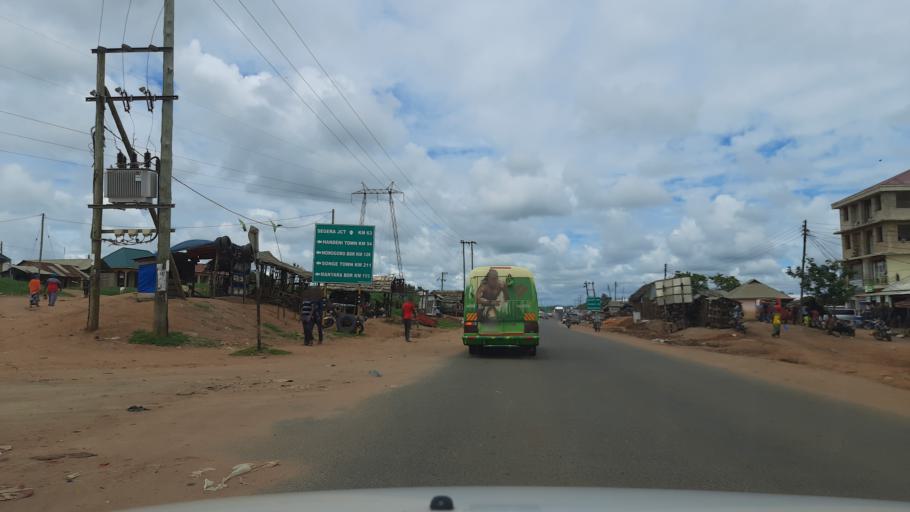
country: TZ
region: Tanga
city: Chanika
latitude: -5.7876
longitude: 38.2906
